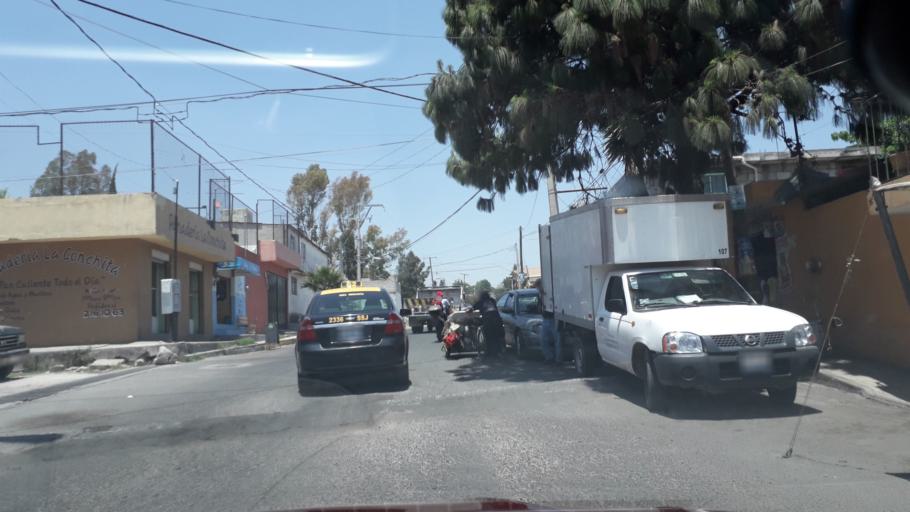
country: MX
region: Puebla
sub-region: Puebla
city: Galaxia la Calera
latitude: 18.9934
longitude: -98.1834
